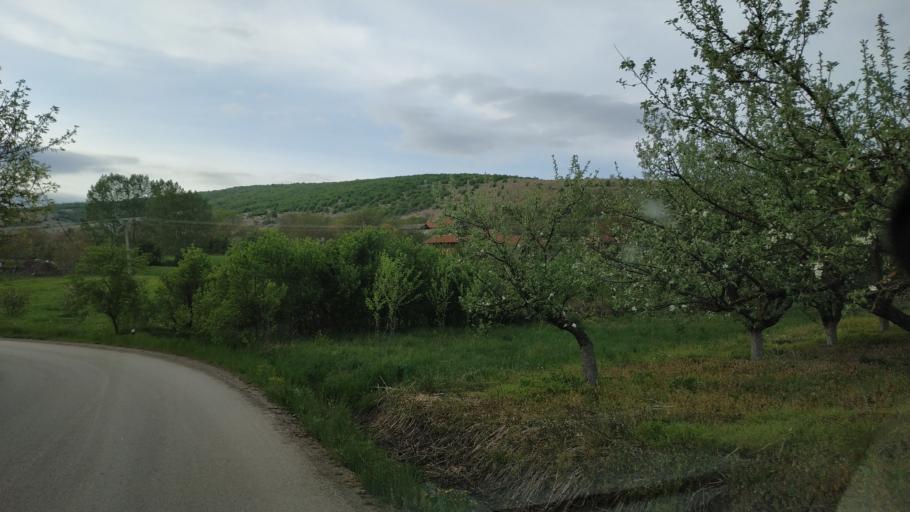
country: RS
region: Central Serbia
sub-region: Zajecarski Okrug
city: Soko Banja
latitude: 43.5251
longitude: 21.8604
